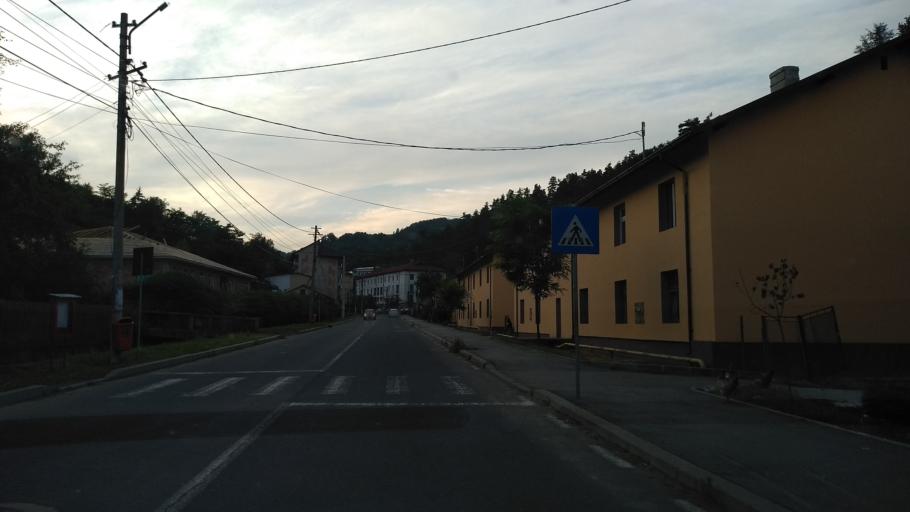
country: RO
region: Hunedoara
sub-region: Comuna Aninoasa
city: Aninoasa
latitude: 45.4050
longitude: 23.3202
